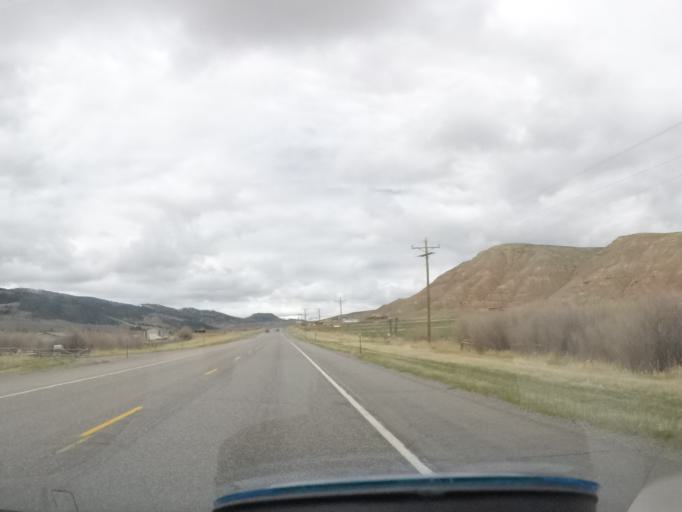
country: US
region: Wyoming
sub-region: Sublette County
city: Pinedale
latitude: 43.5685
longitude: -109.7118
